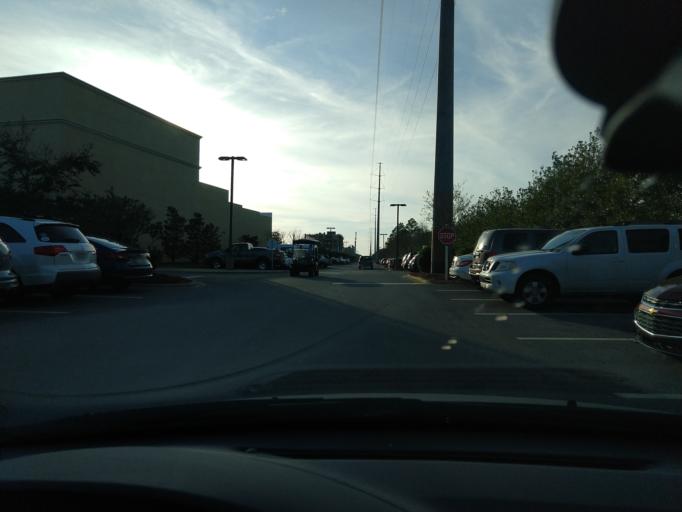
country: US
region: Florida
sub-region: Walton County
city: Miramar Beach
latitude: 30.3802
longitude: -86.3147
